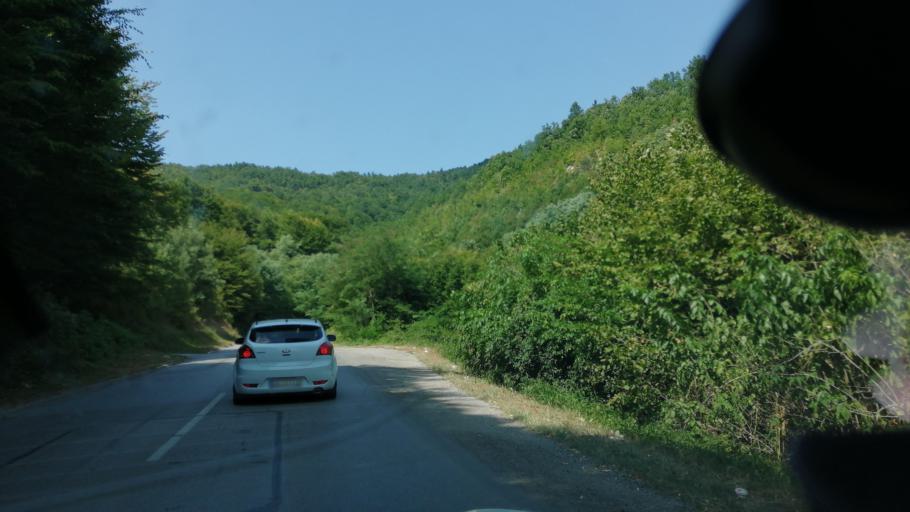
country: RS
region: Central Serbia
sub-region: Moravicki Okrug
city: Ivanjica
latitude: 43.6170
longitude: 20.2358
